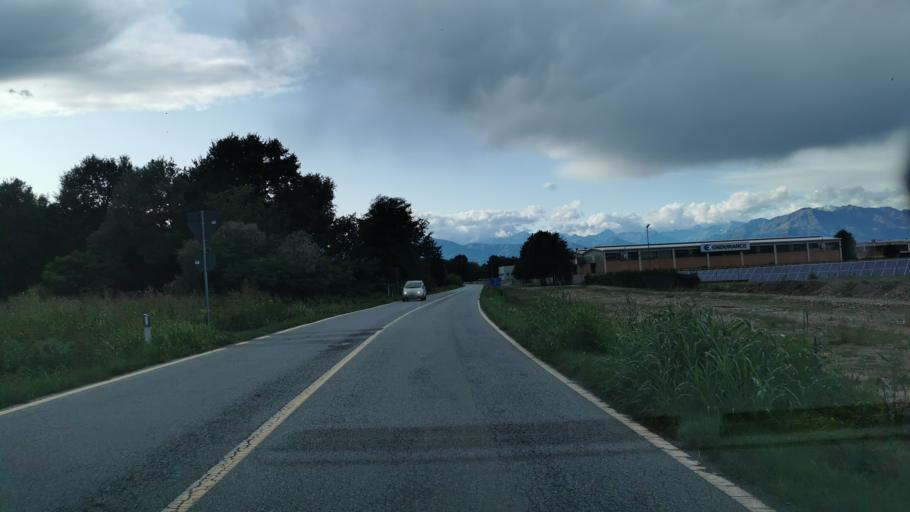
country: IT
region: Piedmont
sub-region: Provincia di Torino
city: Lombardore
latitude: 45.2291
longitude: 7.7537
